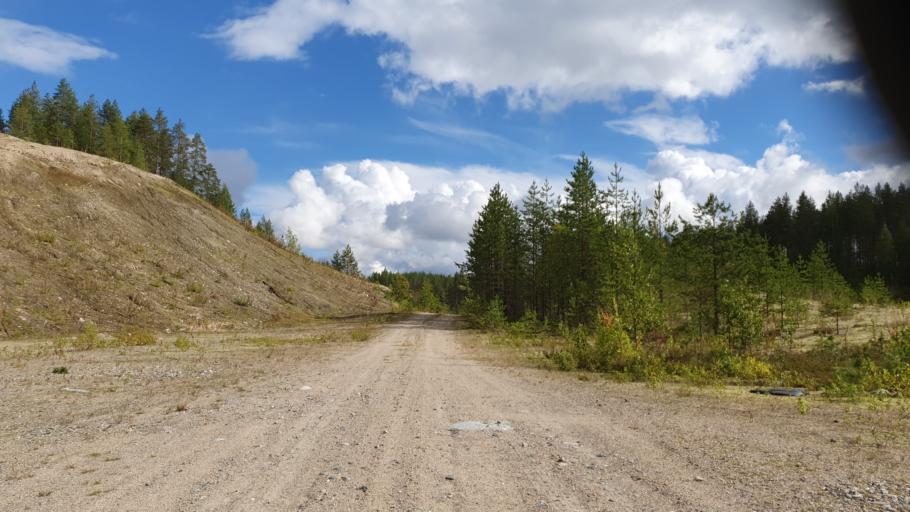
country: FI
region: Kainuu
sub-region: Kehys-Kainuu
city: Kuhmo
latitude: 64.1529
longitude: 29.3812
